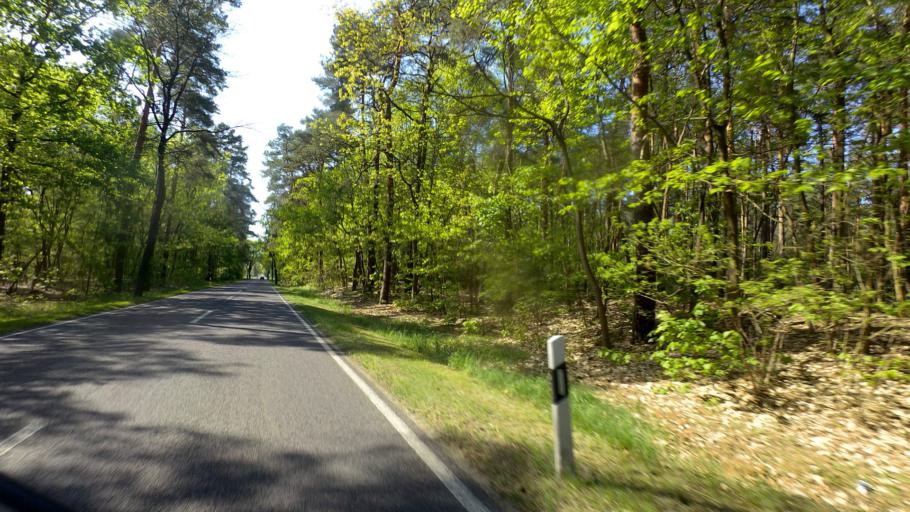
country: DE
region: Brandenburg
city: Munchehofe
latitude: 52.1064
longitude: 13.7811
